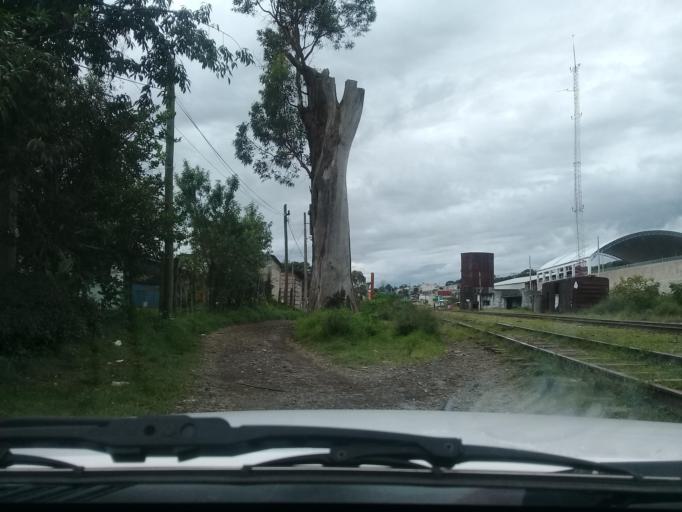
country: MX
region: Veracruz
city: Rafael Lucio
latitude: 19.5986
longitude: -96.9886
